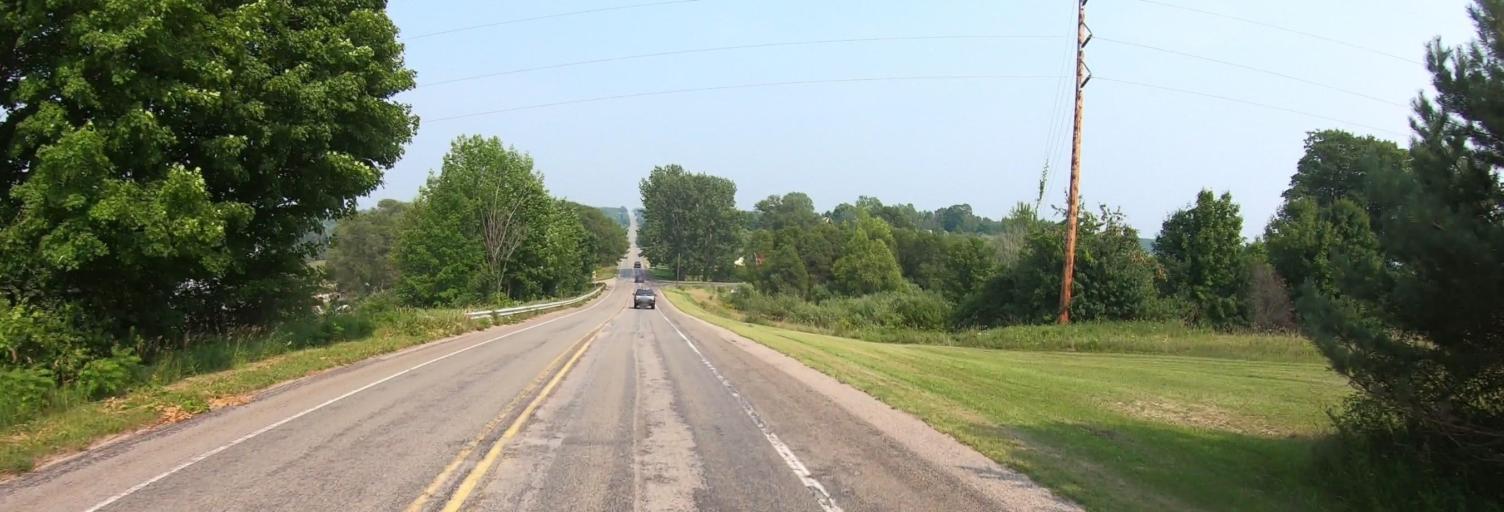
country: US
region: Michigan
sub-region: Charlevoix County
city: Charlevoix
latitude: 45.1857
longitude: -85.3266
